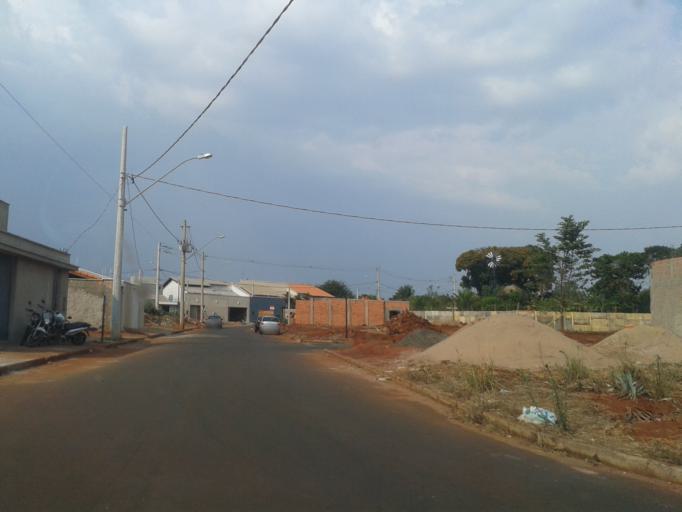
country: BR
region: Minas Gerais
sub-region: Ituiutaba
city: Ituiutaba
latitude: -18.9790
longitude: -49.4838
